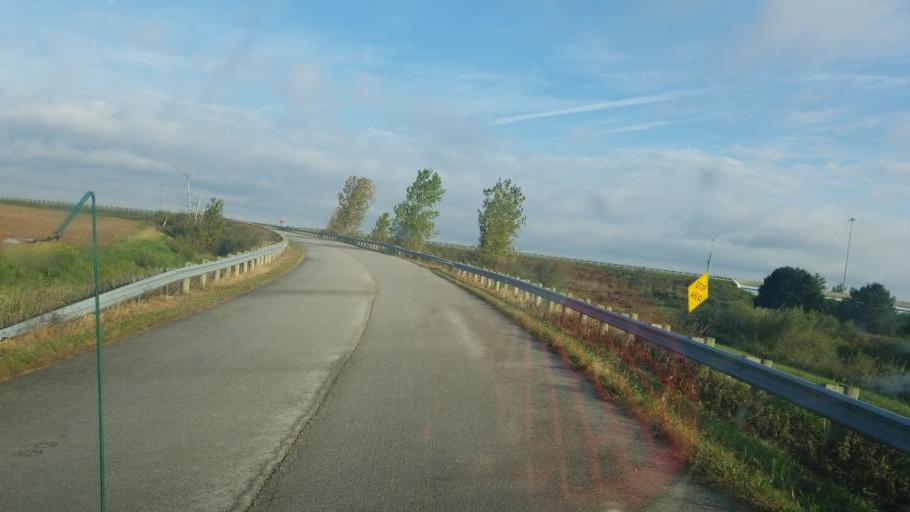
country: US
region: Ohio
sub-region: Wyandot County
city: Upper Sandusky
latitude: 40.8596
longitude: -83.3234
